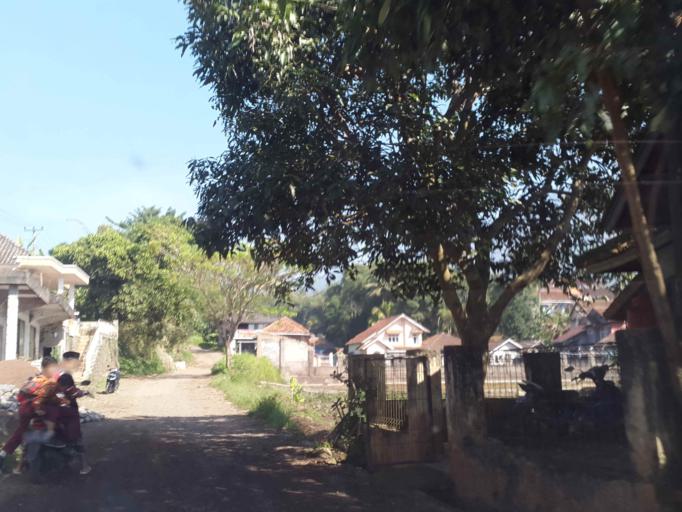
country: ID
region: West Java
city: Sukabumi
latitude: -6.8467
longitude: 107.0569
